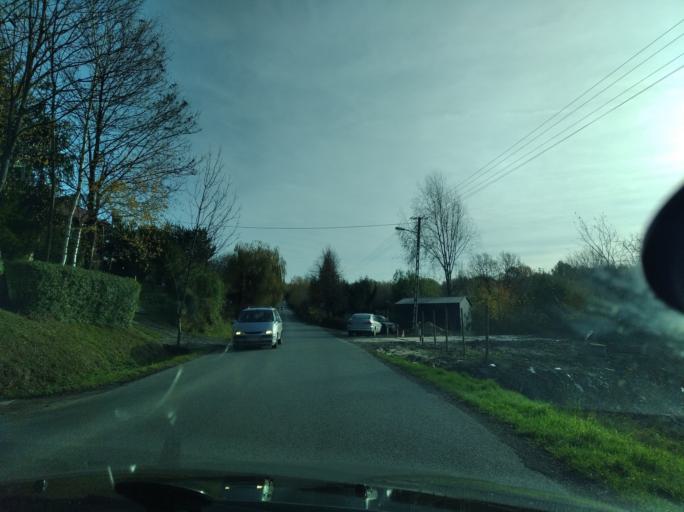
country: PL
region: Subcarpathian Voivodeship
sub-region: Powiat rzeszowski
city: Tyczyn
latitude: 49.9943
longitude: 22.0603
